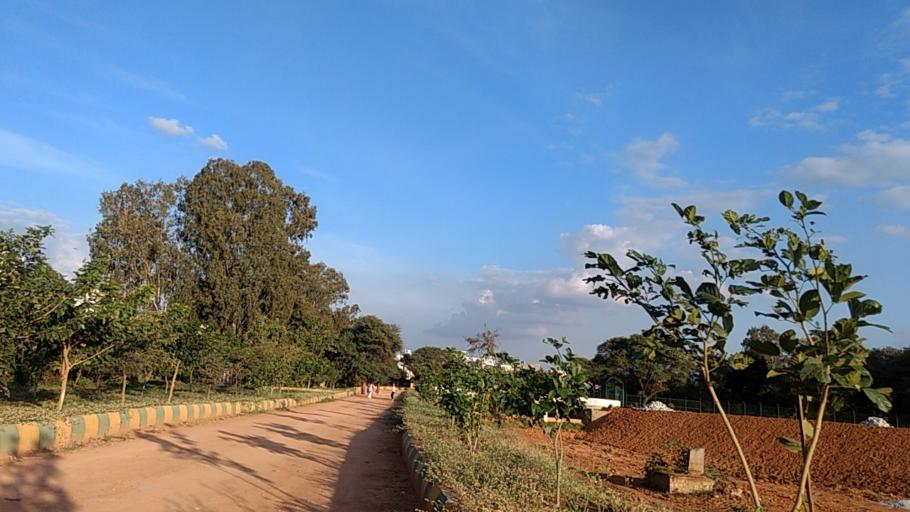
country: IN
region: Karnataka
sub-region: Bangalore Urban
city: Yelahanka
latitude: 13.0636
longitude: 77.5669
